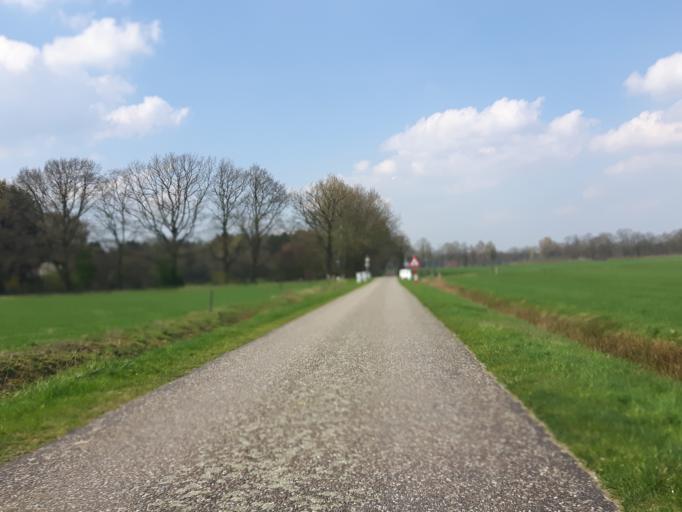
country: NL
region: Overijssel
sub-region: Gemeente Enschede
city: Enschede
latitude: 52.1863
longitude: 6.8281
